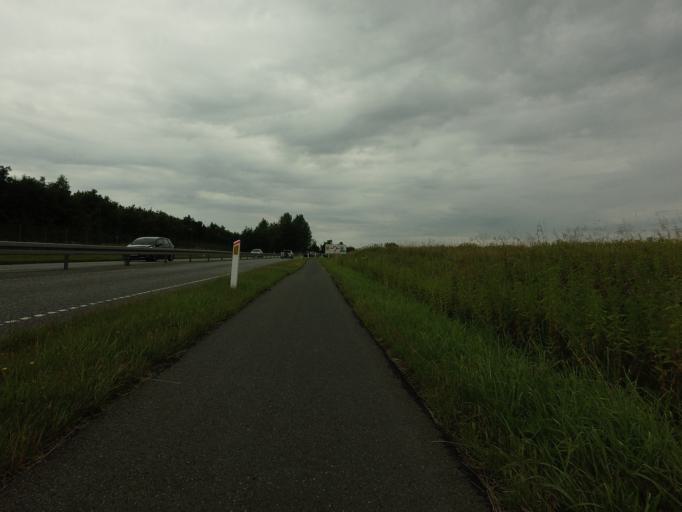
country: DK
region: North Denmark
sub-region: Alborg Kommune
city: Vadum
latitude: 57.1000
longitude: 9.8851
